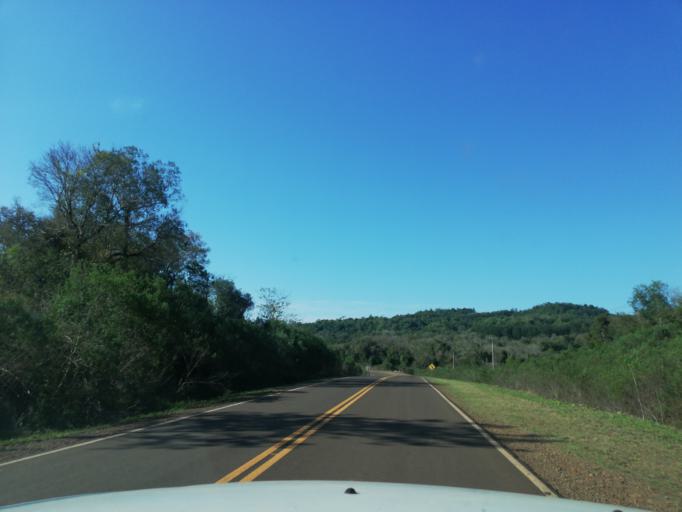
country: AR
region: Misiones
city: Arroyo del Medio
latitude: -27.6883
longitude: -55.3978
